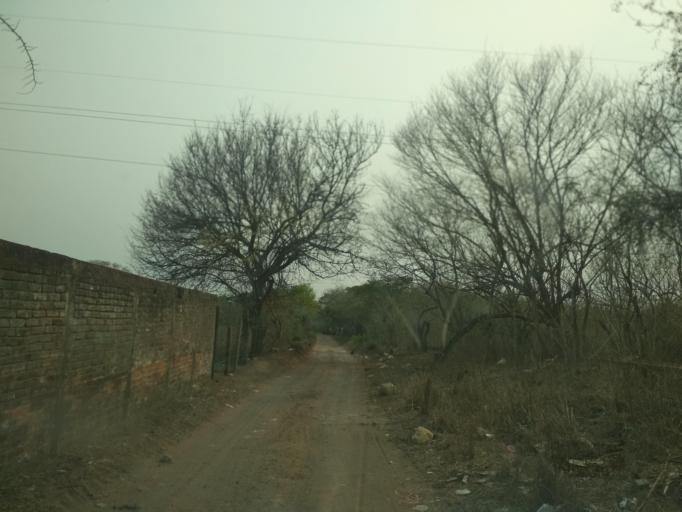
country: MX
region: Veracruz
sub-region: Veracruz
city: Delfino Victoria (Santa Fe)
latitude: 19.1911
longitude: -96.2993
